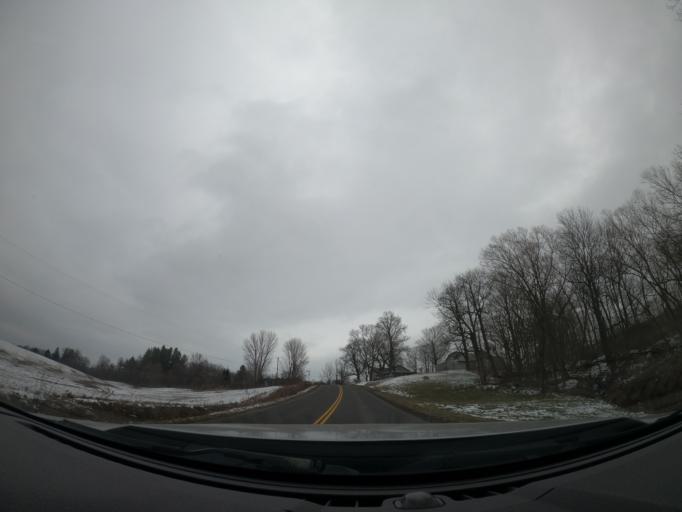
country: US
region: New York
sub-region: Cayuga County
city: Moravia
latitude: 42.7362
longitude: -76.3905
